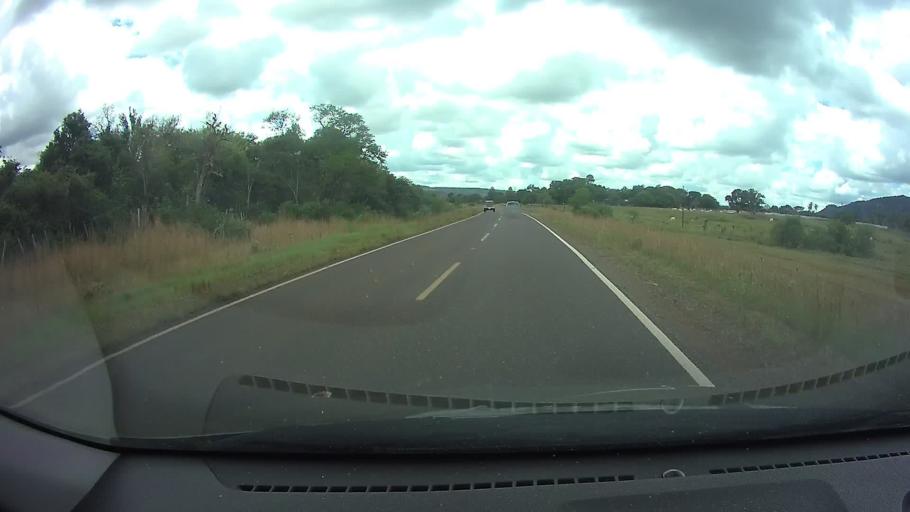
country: PY
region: Paraguari
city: Ybycui
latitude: -25.9083
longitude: -56.9827
